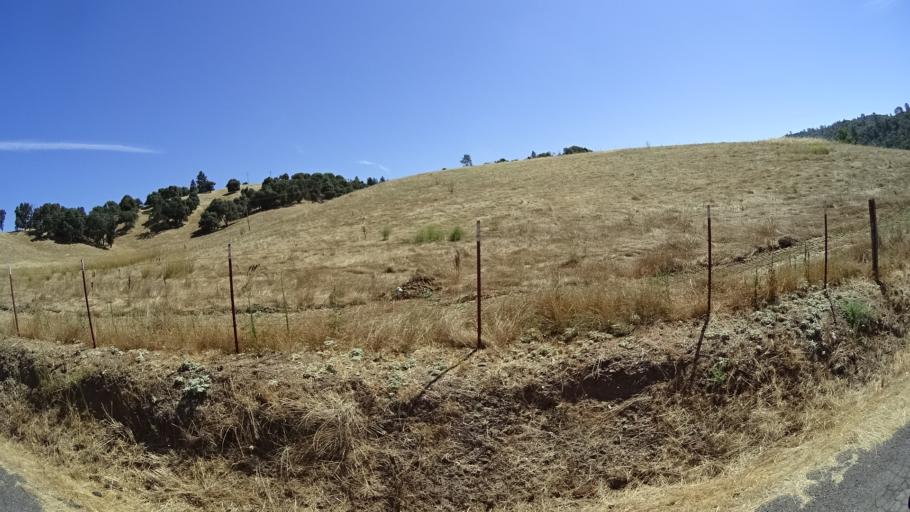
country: US
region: California
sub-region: Calaveras County
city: Angels Camp
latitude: 38.1430
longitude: -120.5513
